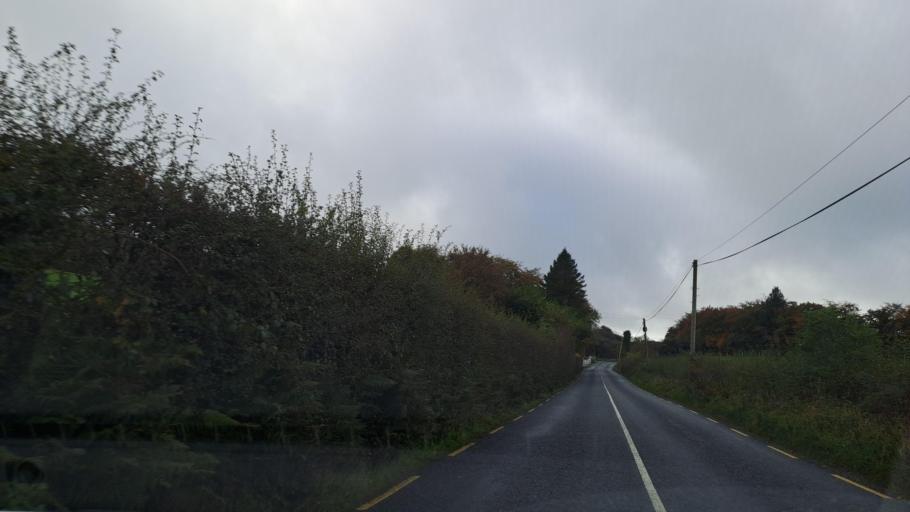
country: IE
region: Ulster
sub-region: An Cabhan
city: Bailieborough
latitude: 53.8992
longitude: -7.0078
